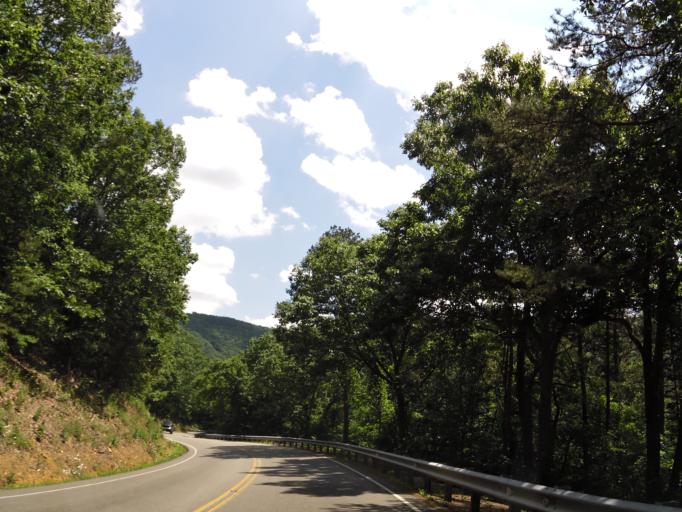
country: US
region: Tennessee
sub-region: Bledsoe County
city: Pikeville
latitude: 35.5750
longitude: -85.1544
